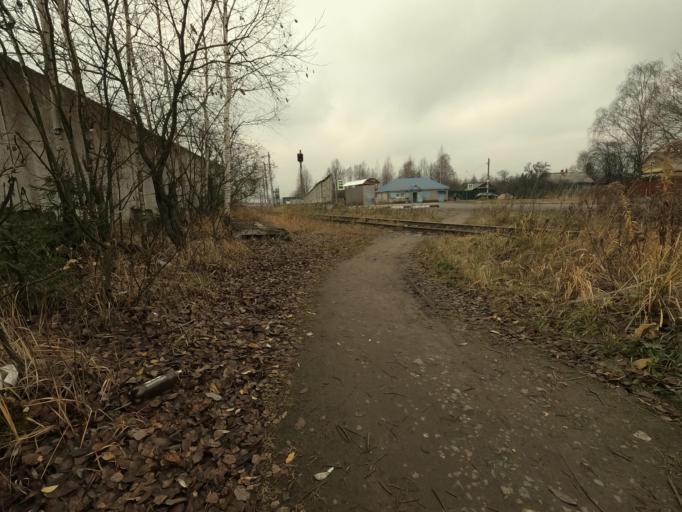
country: RU
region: Leningrad
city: Lyuban'
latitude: 59.4936
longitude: 31.2738
